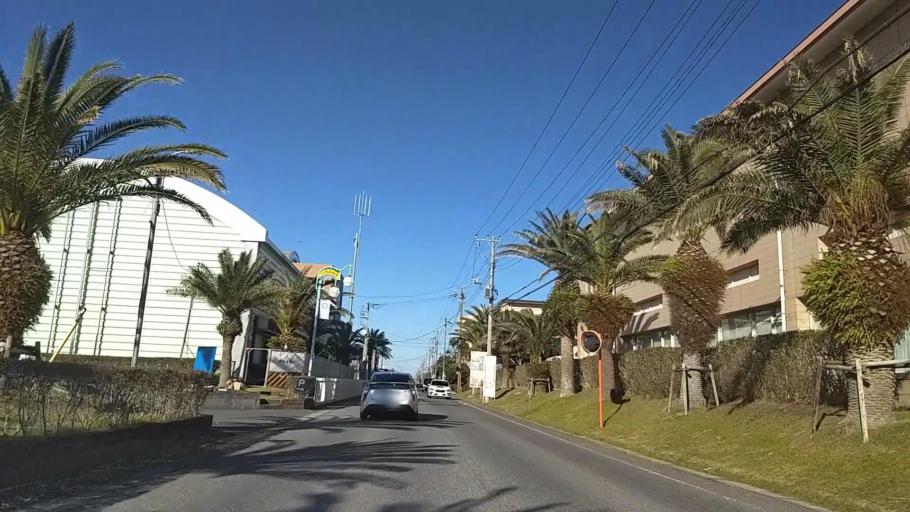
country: JP
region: Chiba
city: Mobara
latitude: 35.3616
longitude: 140.3880
